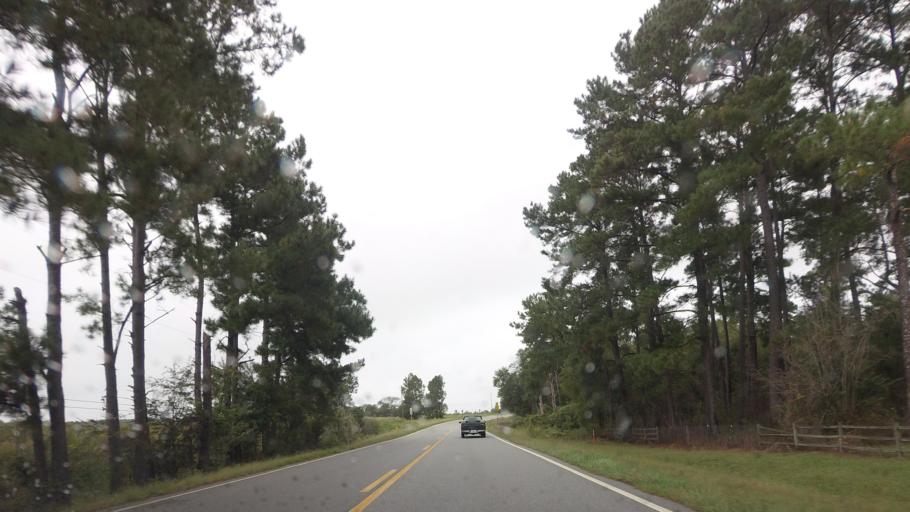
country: US
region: Georgia
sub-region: Berrien County
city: Enigma
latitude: 31.4247
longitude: -83.2474
